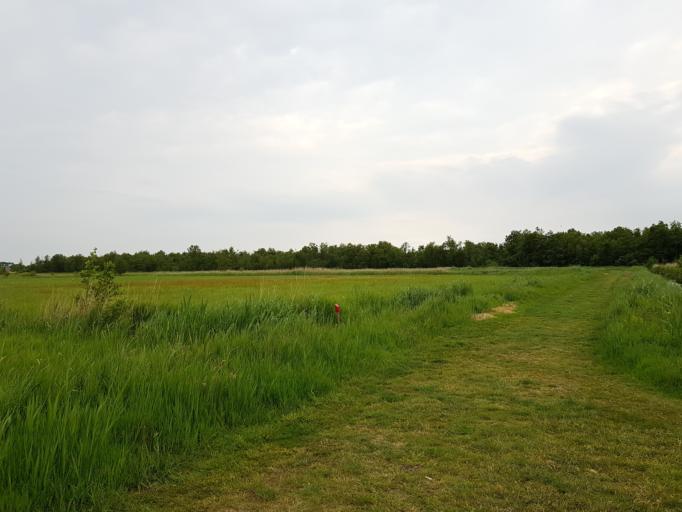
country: NL
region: Friesland
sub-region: Gemeente Tytsjerksteradiel
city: Garyp
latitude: 53.1414
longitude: 5.9400
